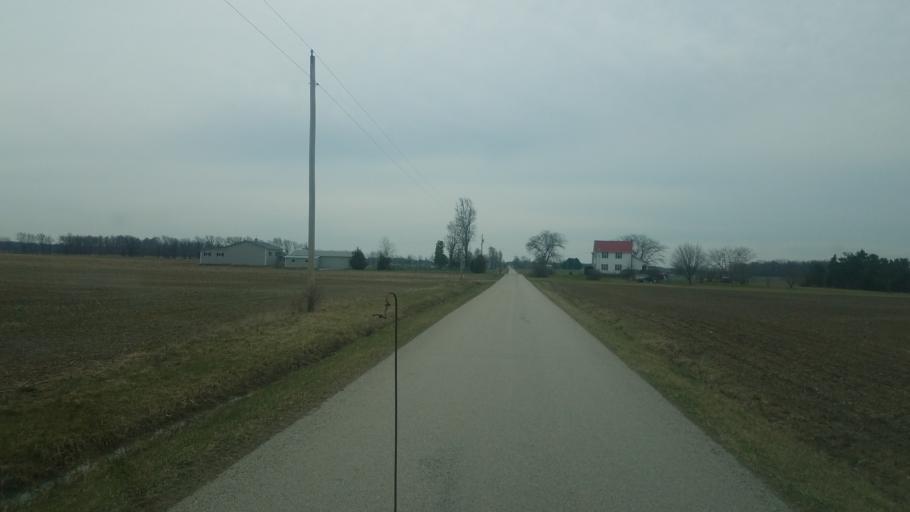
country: US
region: Ohio
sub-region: Huron County
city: Greenwich
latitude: 41.1290
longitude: -82.5646
